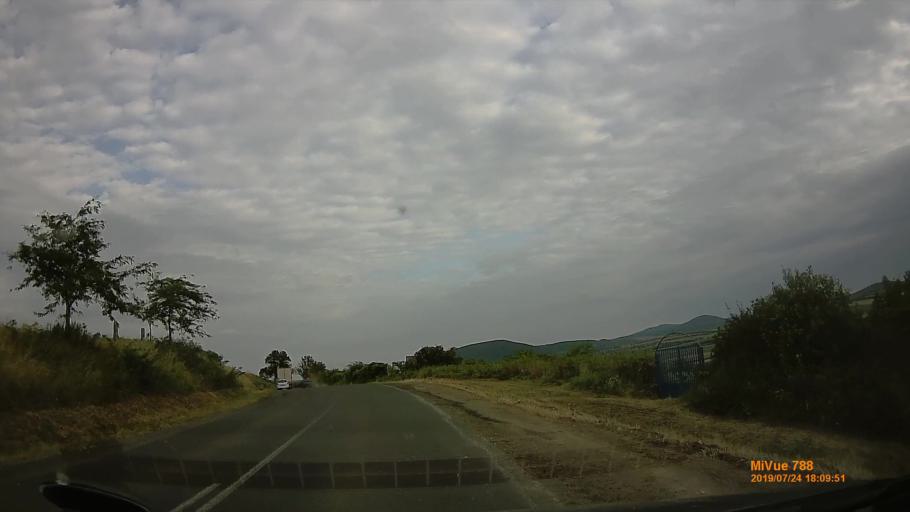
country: HU
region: Borsod-Abauj-Zemplen
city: Abaujszanto
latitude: 48.2652
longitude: 21.1847
